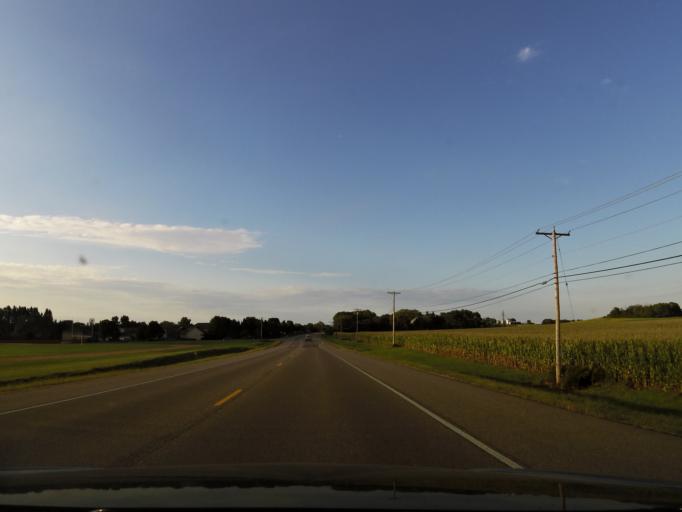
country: US
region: Minnesota
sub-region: Washington County
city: Cottage Grove
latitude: 44.8385
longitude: -92.9035
